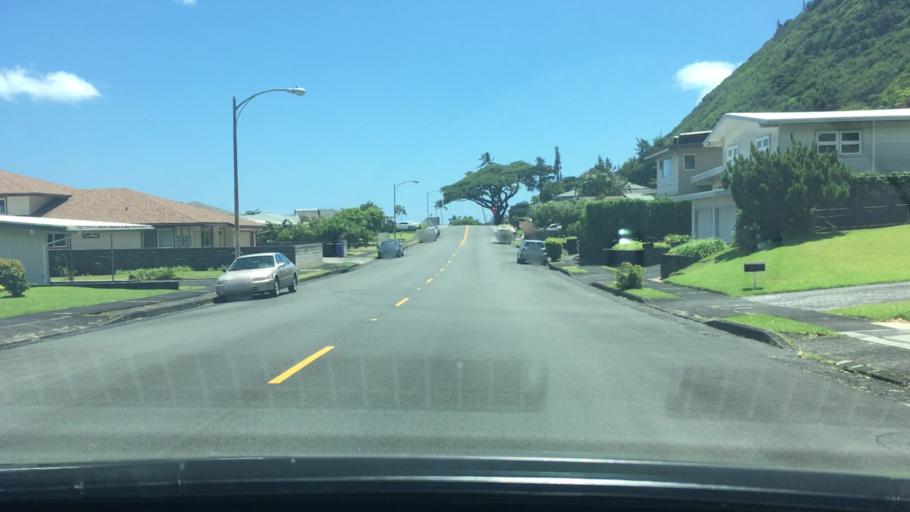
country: US
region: Hawaii
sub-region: Honolulu County
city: Honolulu
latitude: 21.3215
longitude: -157.8071
